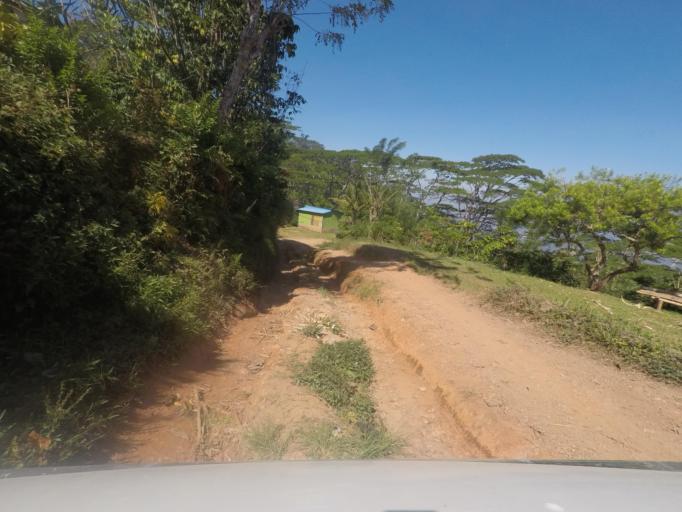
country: TL
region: Ermera
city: Gleno
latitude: -8.7232
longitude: 125.3260
